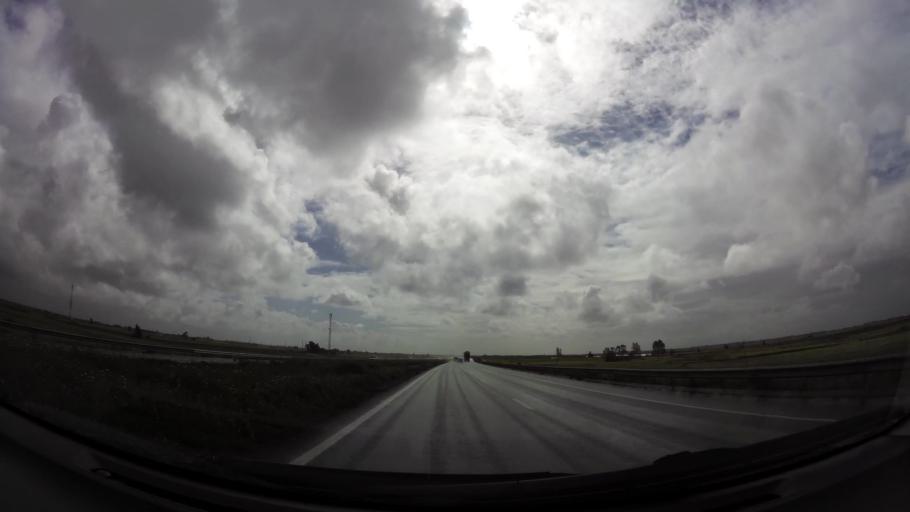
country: MA
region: Grand Casablanca
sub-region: Nouaceur
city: Dar Bouazza
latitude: 33.3664
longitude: -7.9278
